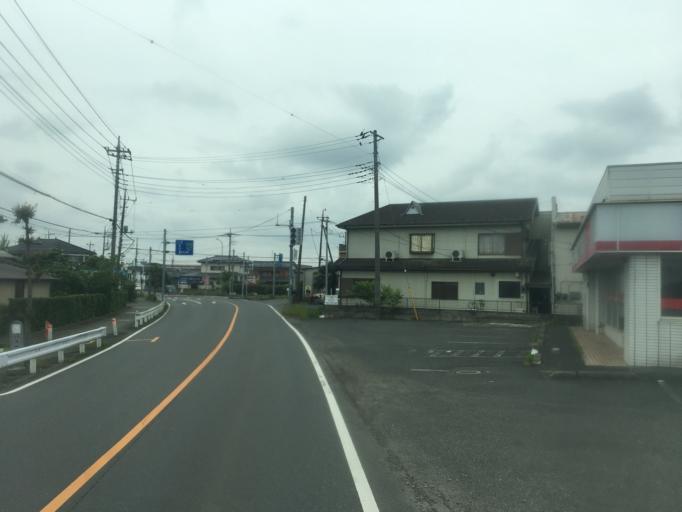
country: JP
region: Saitama
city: Kawagoe
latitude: 35.9705
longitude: 139.4630
